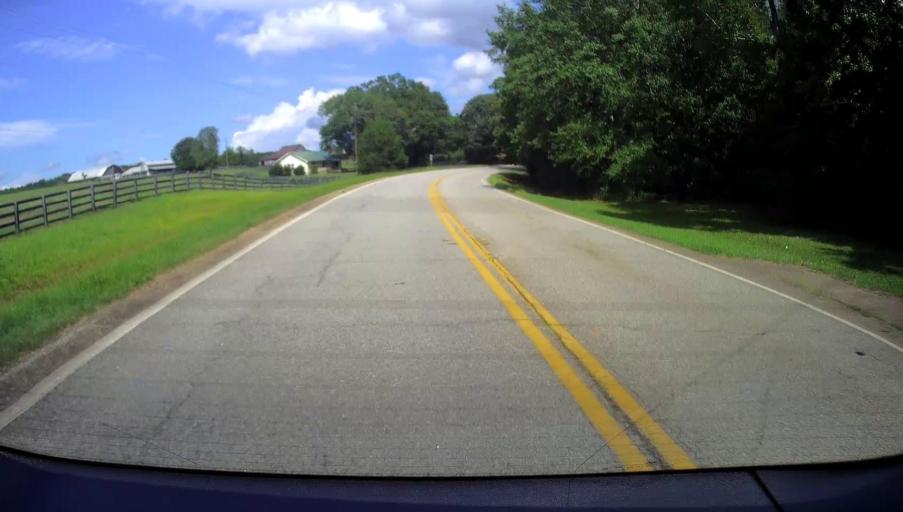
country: US
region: Georgia
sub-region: Crawford County
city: Knoxville
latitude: 32.8844
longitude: -84.0072
